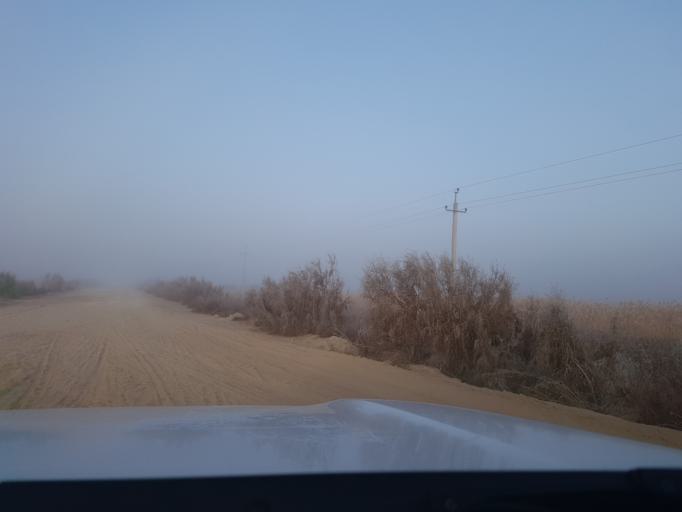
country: TM
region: Dasoguz
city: Koeneuergench
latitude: 41.8453
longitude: 58.4323
